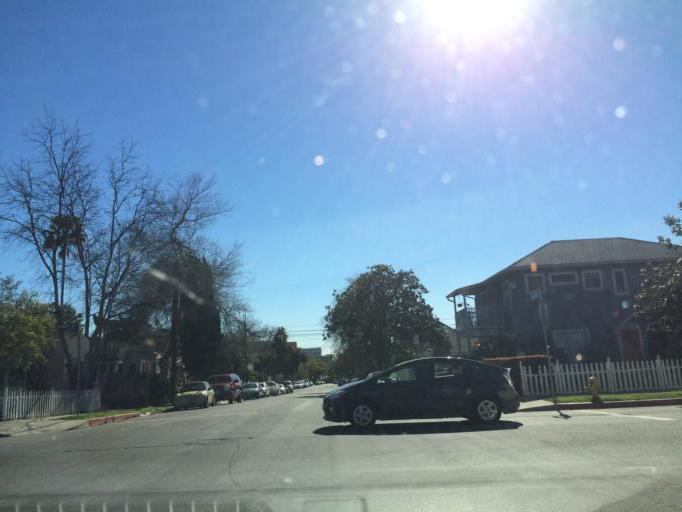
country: US
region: California
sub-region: Los Angeles County
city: Silver Lake
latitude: 34.1037
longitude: -118.2896
